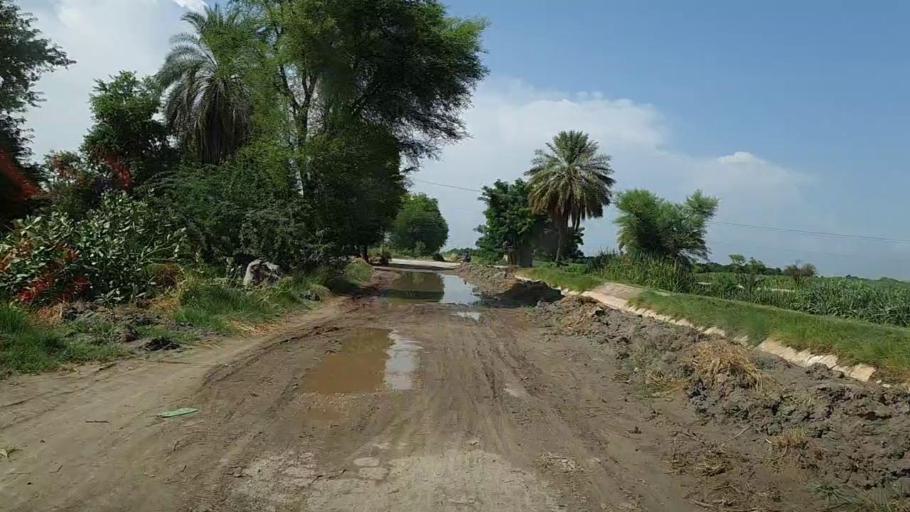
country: PK
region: Sindh
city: Bhiria
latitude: 26.8947
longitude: 68.2370
